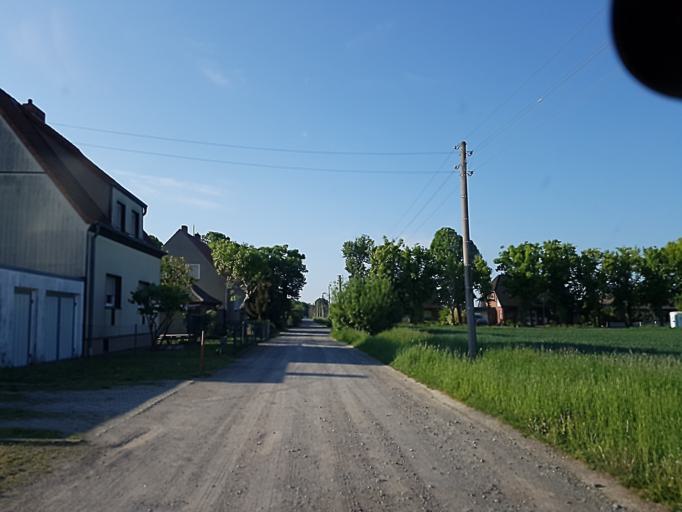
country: DE
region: Brandenburg
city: Doberlug-Kirchhain
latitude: 51.6385
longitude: 13.5519
